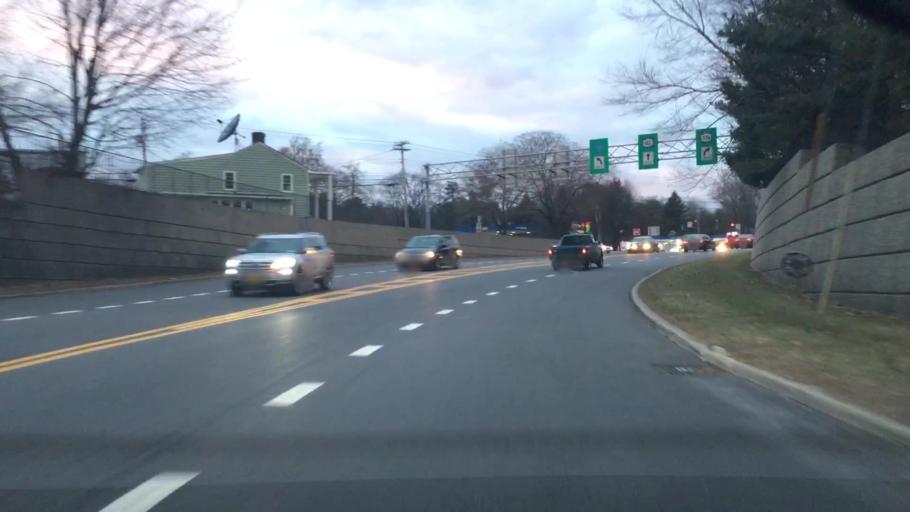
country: US
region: New York
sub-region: Dutchess County
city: Red Oaks Mill
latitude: 41.6544
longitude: -73.8736
